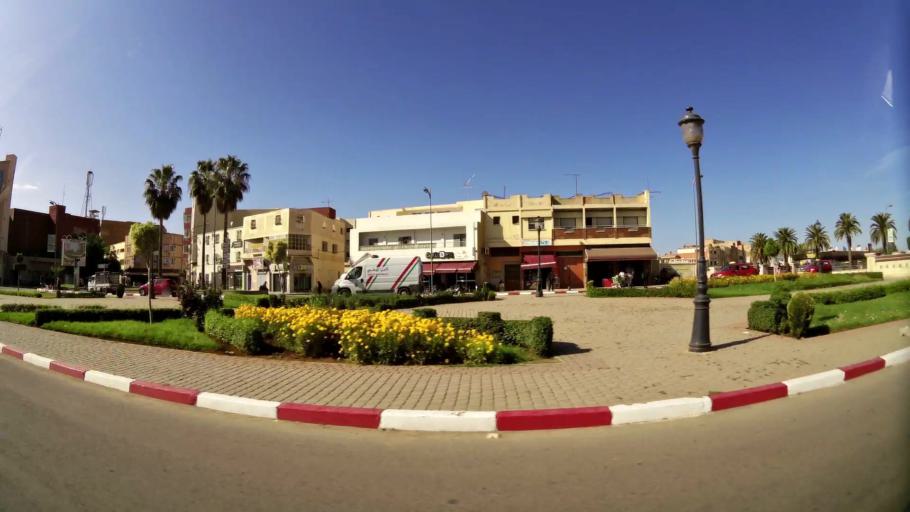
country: MA
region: Oriental
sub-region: Oujda-Angad
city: Oujda
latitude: 34.6759
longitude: -1.9261
